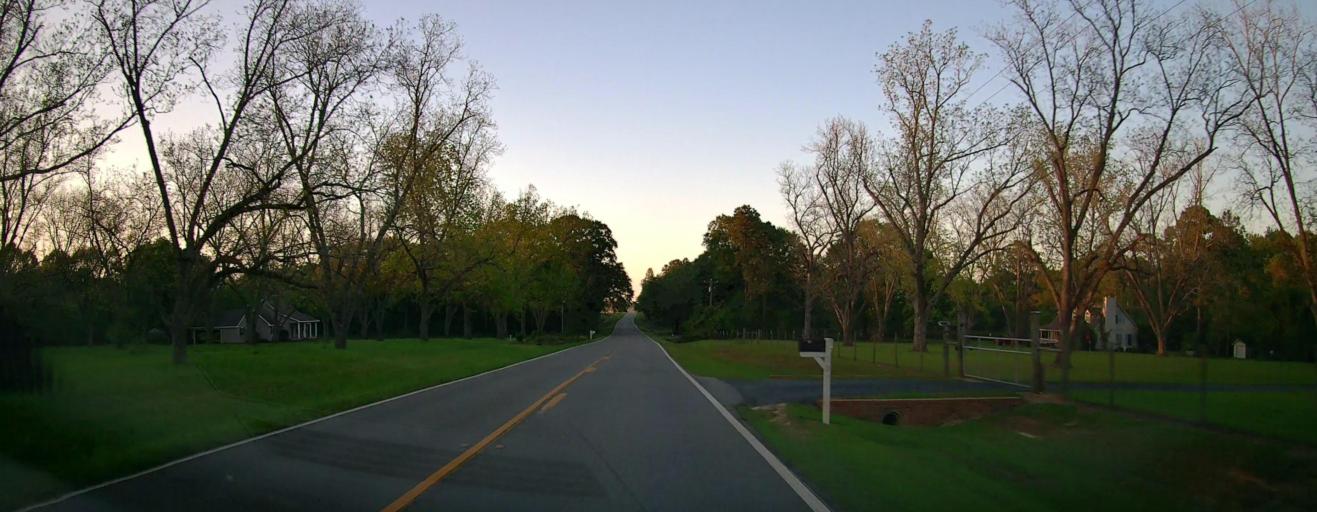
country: US
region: Georgia
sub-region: Ben Hill County
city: Fitzgerald
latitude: 31.7205
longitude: -83.3099
